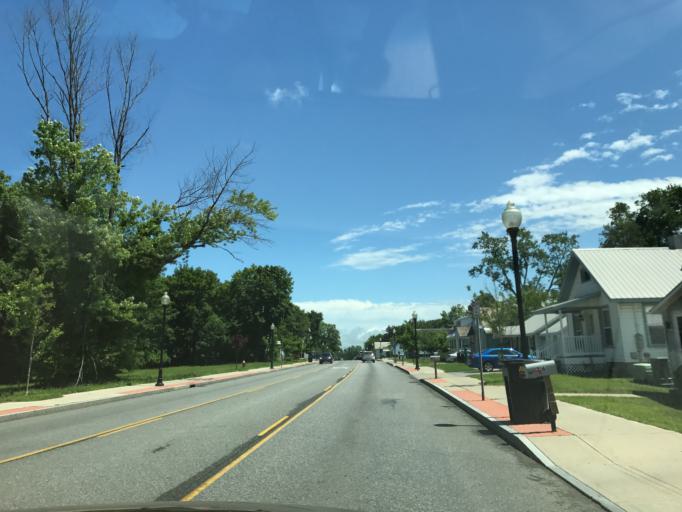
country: US
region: New York
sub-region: Warren County
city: West Glens Falls
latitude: 43.2994
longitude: -73.6715
